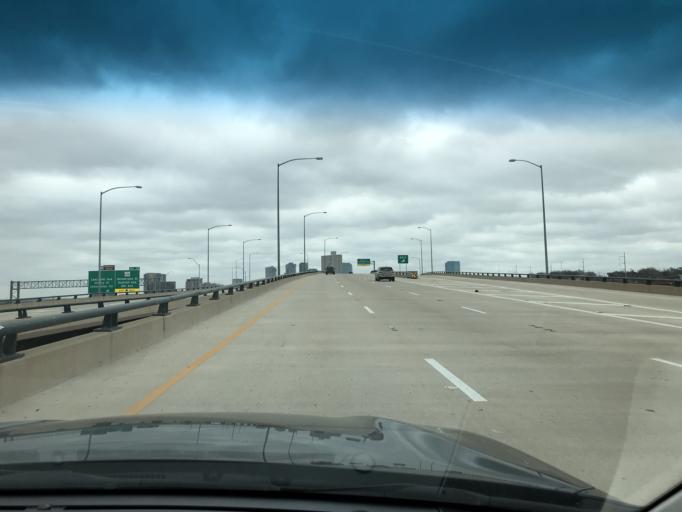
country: US
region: Texas
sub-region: Tarrant County
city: Fort Worth
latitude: 32.7363
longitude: -97.3535
